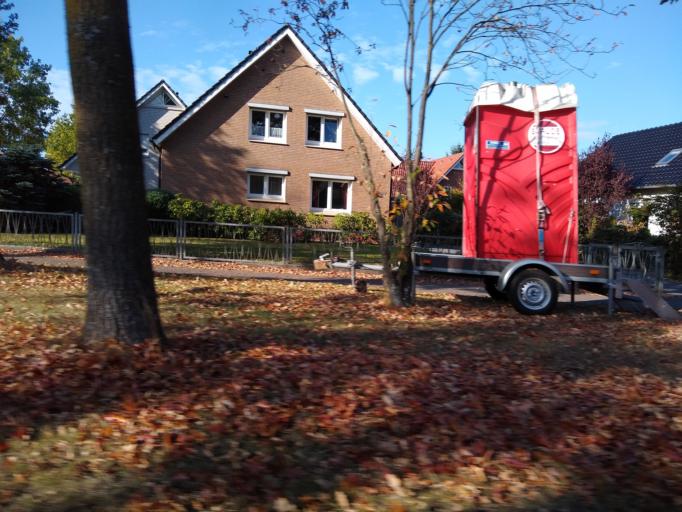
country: DE
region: Lower Saxony
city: Oldenburg
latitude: 53.1806
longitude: 8.2056
